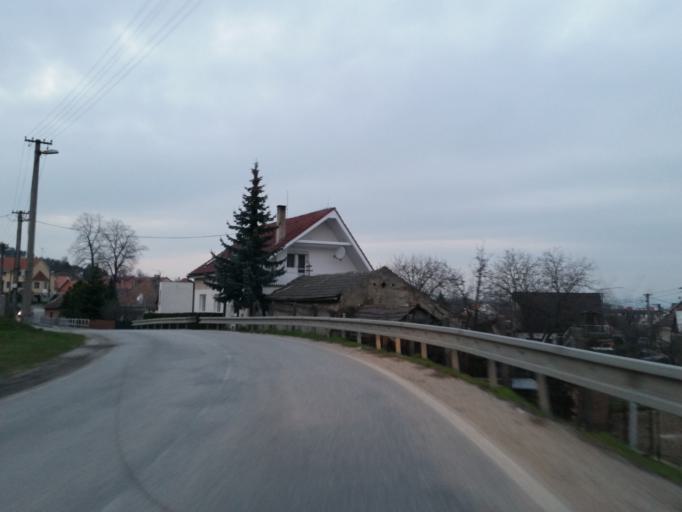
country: SK
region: Trnavsky
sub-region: Okres Trnava
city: Piestany
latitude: 48.5812
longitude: 17.8523
